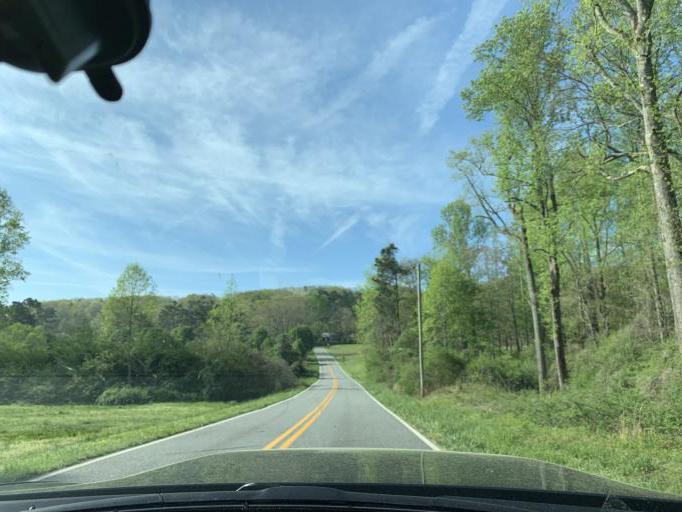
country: US
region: Georgia
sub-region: Forsyth County
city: Cumming
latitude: 34.2577
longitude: -84.1225
